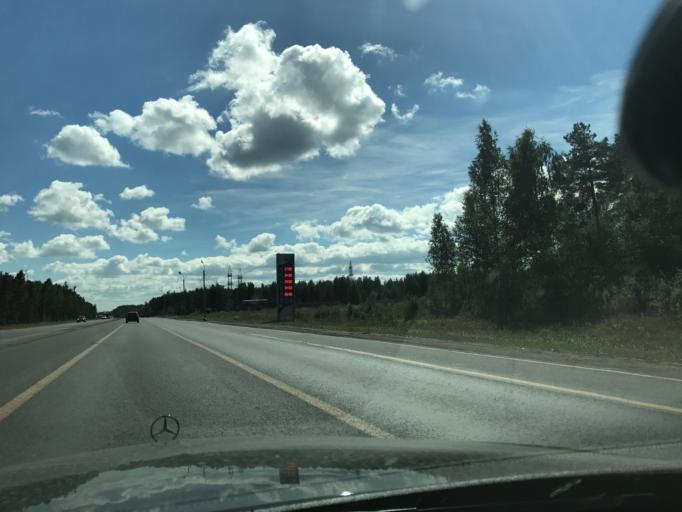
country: RU
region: Nizjnij Novgorod
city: Gorbatovka
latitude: 56.2764
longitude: 43.7015
